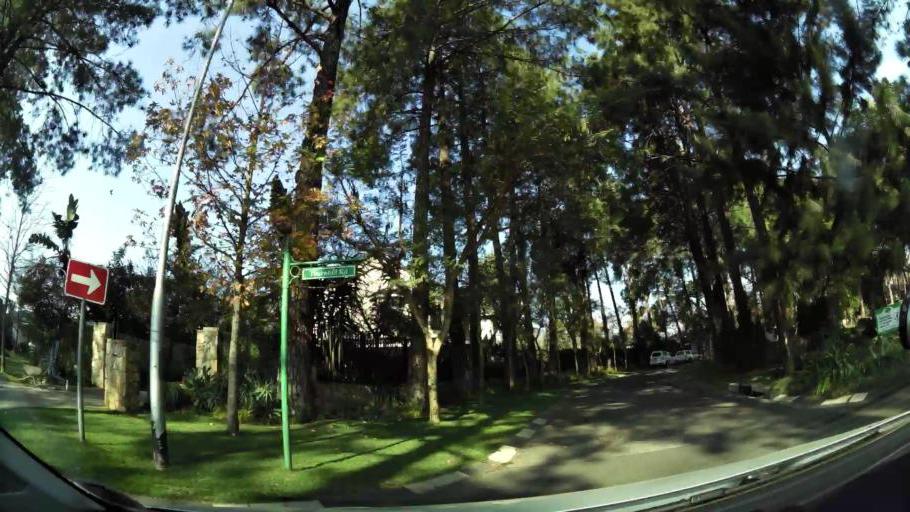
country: ZA
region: Gauteng
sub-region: City of Johannesburg Metropolitan Municipality
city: Modderfontein
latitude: -26.1037
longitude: 28.1546
